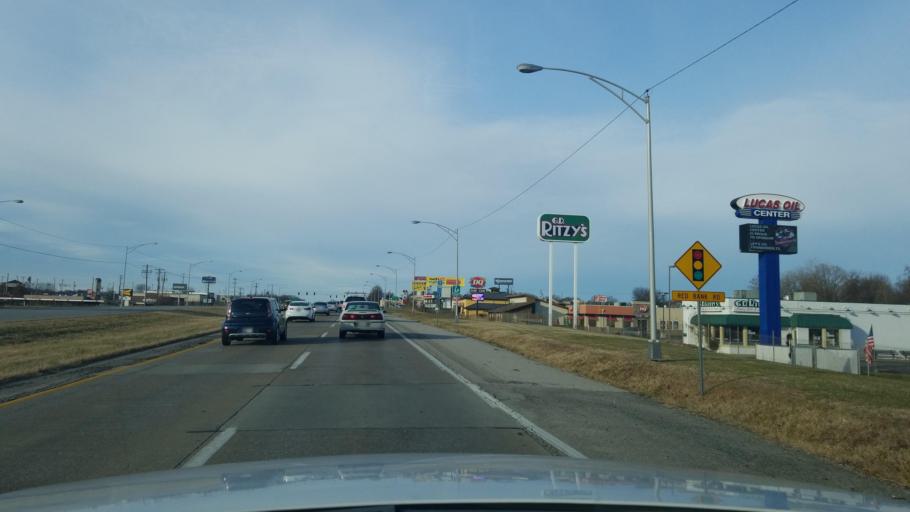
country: US
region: Indiana
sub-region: Vanderburgh County
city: Evansville
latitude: 37.9774
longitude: -87.6330
